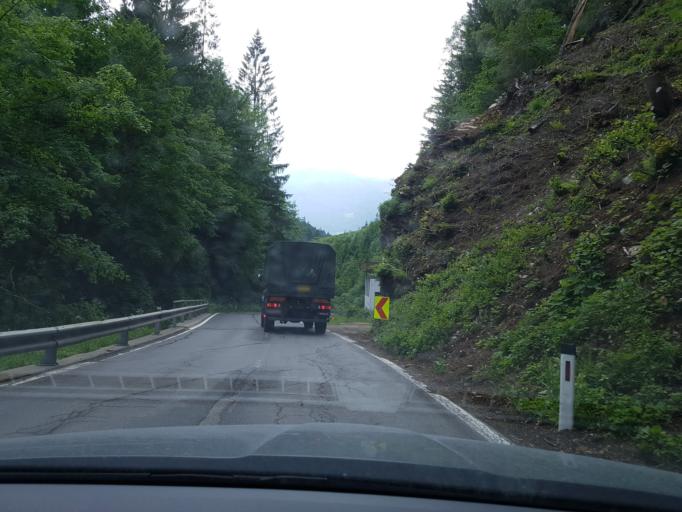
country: AT
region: Carinthia
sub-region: Politischer Bezirk Villach Land
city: Feld am See
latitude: 46.8017
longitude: 13.7535
